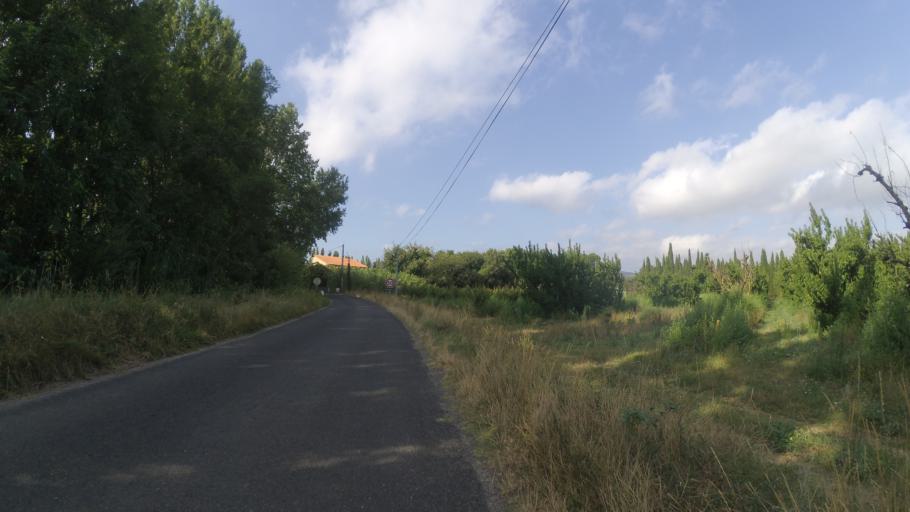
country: FR
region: Languedoc-Roussillon
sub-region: Departement des Pyrenees-Orientales
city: Millas
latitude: 42.6607
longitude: 2.7079
